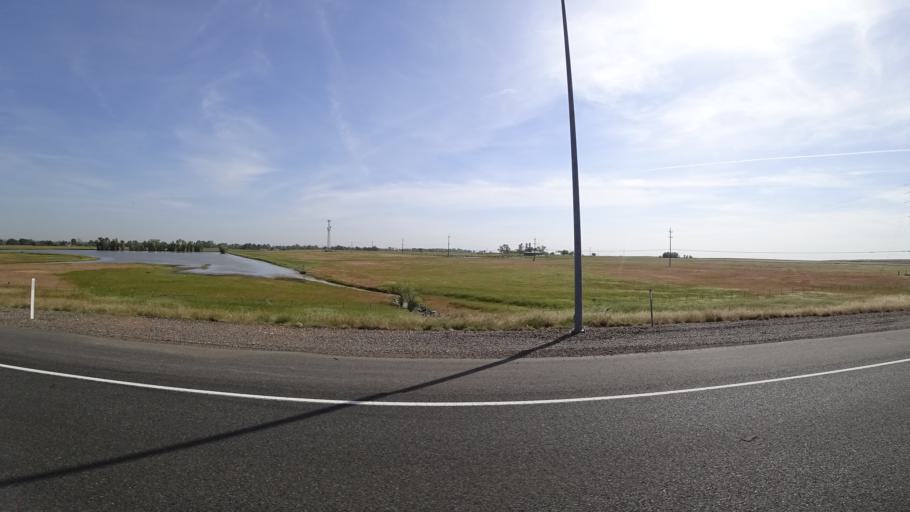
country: US
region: California
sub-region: Butte County
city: Durham
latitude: 39.6174
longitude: -121.6854
